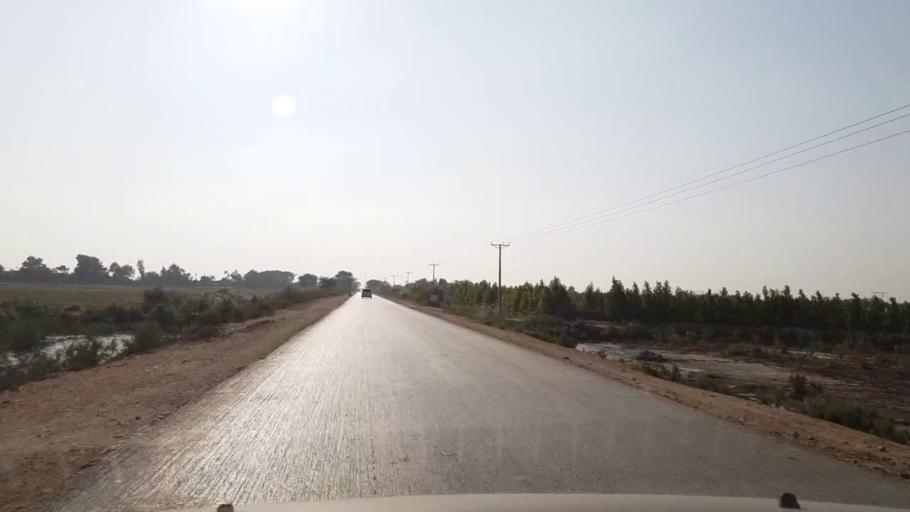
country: PK
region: Sindh
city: Tando Muhammad Khan
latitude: 25.0636
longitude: 68.4664
